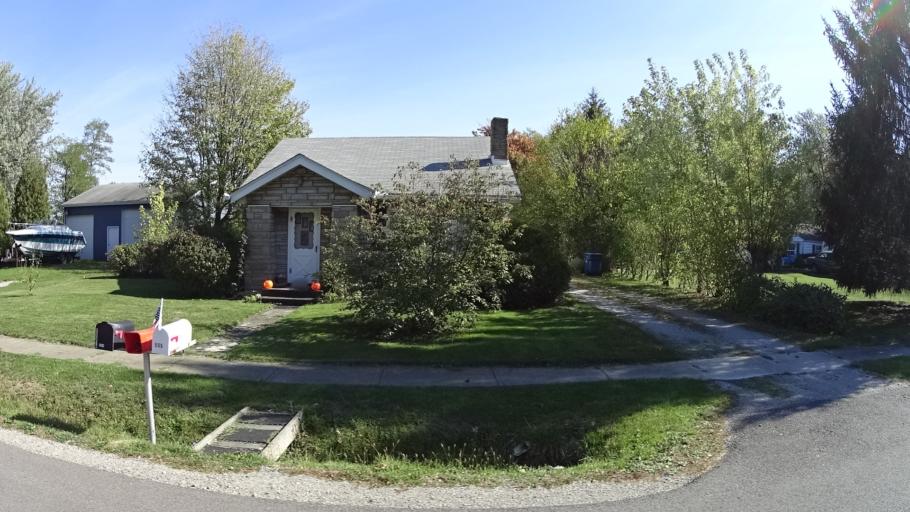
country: US
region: Ohio
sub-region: Lorain County
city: Vermilion-on-the-Lake
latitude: 41.4239
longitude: -82.3103
